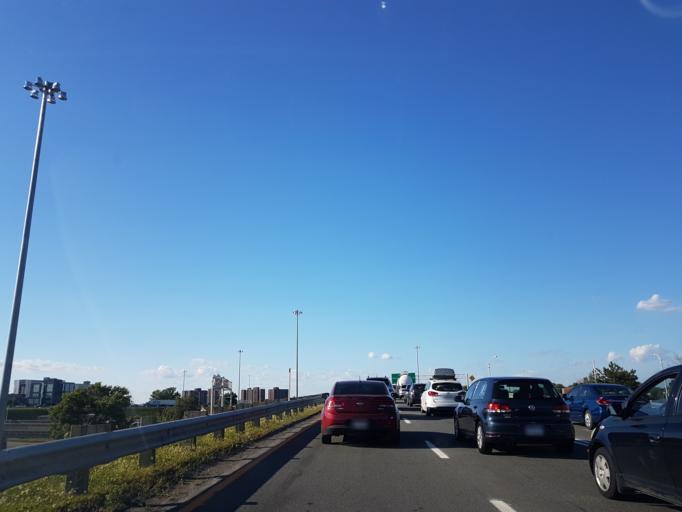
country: CA
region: Quebec
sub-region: Monteregie
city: Longueuil
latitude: 45.5203
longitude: -73.5146
